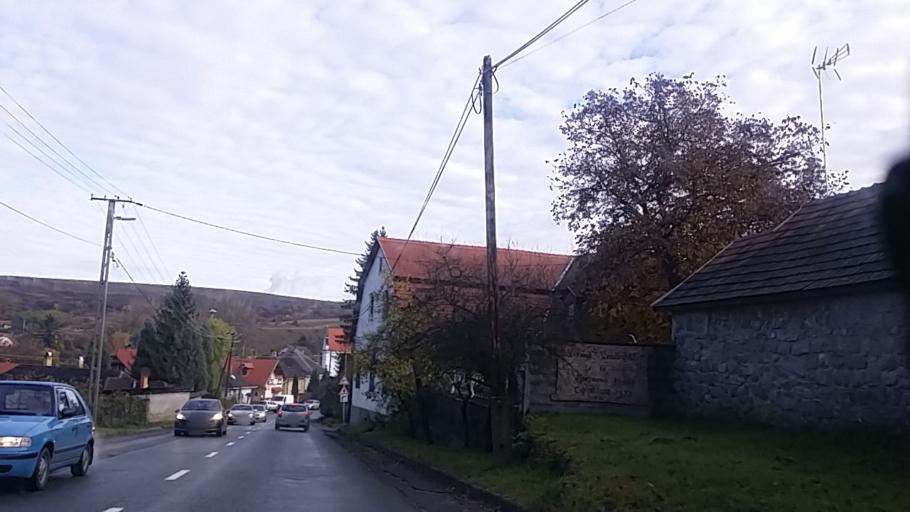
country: HU
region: Heves
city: Szilvasvarad
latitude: 48.1387
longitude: 20.4229
